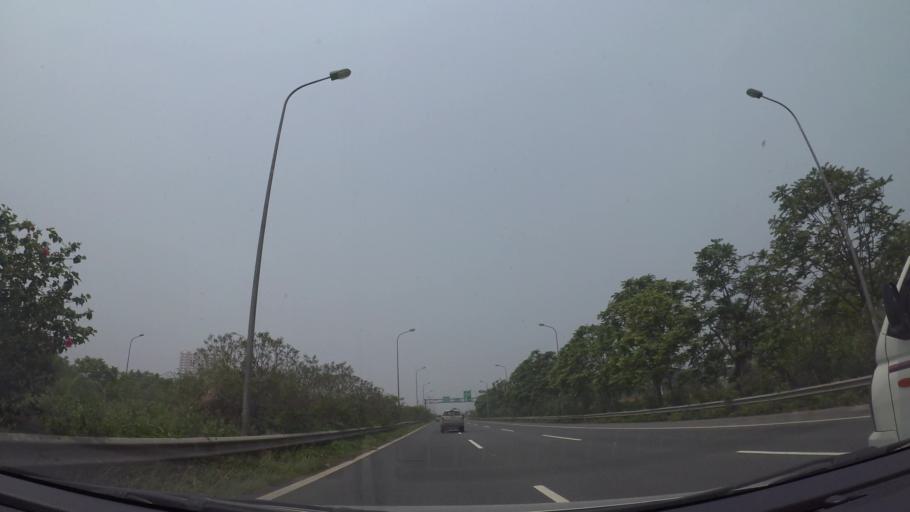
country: VN
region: Ha Noi
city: Lien Quan
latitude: 20.9904
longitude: 105.5344
